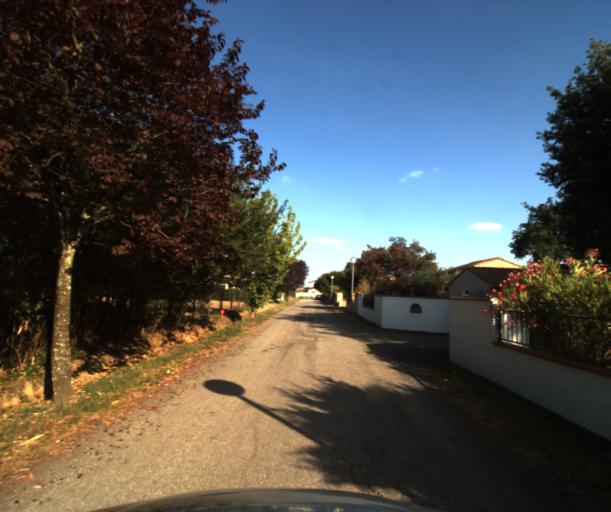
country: FR
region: Midi-Pyrenees
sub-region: Departement de la Haute-Garonne
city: Saint-Lys
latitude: 43.5082
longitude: 1.1912
